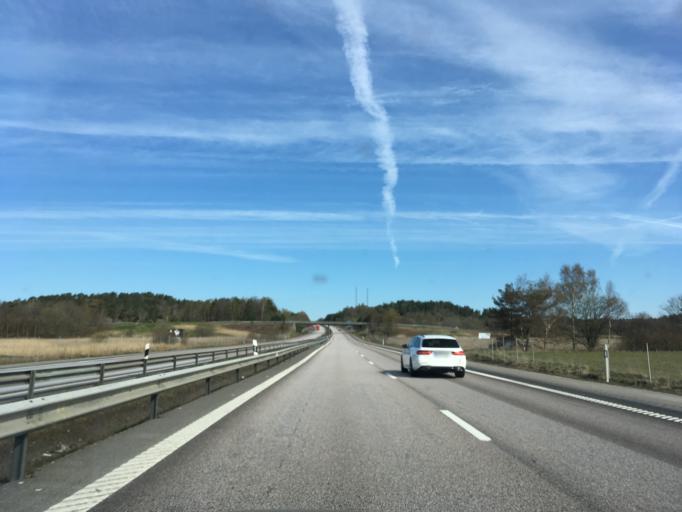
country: SE
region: Halland
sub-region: Kungsbacka Kommun
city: Fjaeras kyrkby
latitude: 57.4164
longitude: 12.1693
